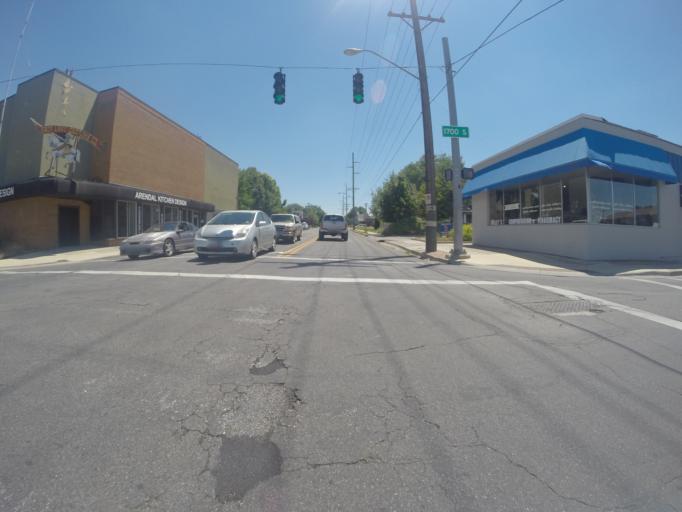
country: US
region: Utah
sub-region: Salt Lake County
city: South Salt Lake
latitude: 40.7336
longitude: -111.8597
